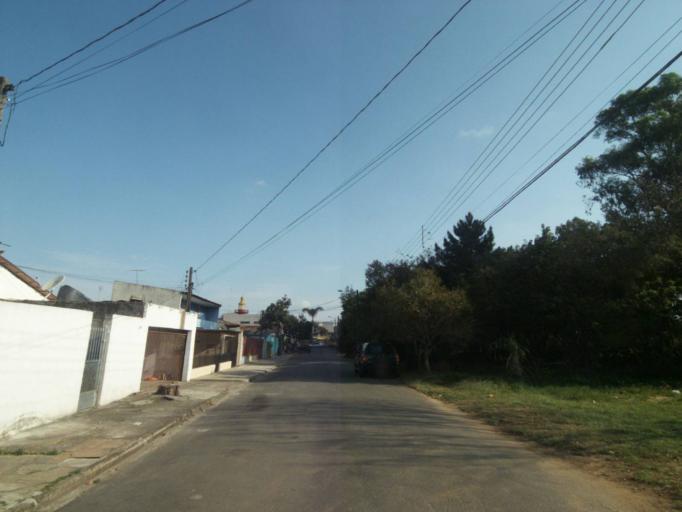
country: BR
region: Parana
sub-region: Curitiba
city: Curitiba
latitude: -25.4933
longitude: -49.3359
